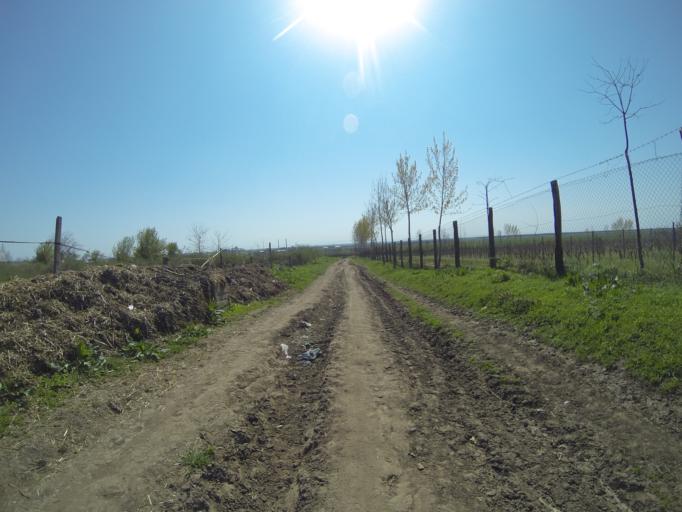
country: RO
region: Dolj
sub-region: Comuna Segarcea
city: Segarcea
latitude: 44.1014
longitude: 23.7256
